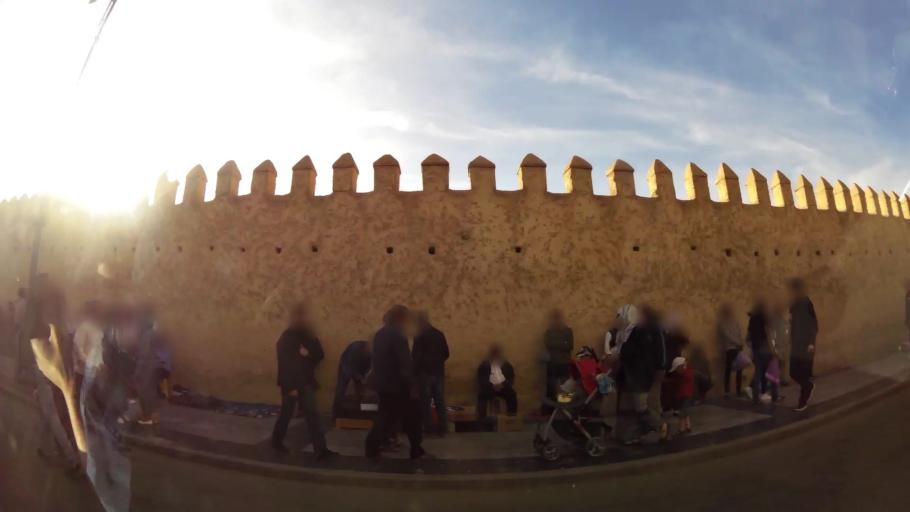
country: MA
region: Oriental
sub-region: Oujda-Angad
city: Oujda
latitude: 34.6794
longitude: -1.9107
